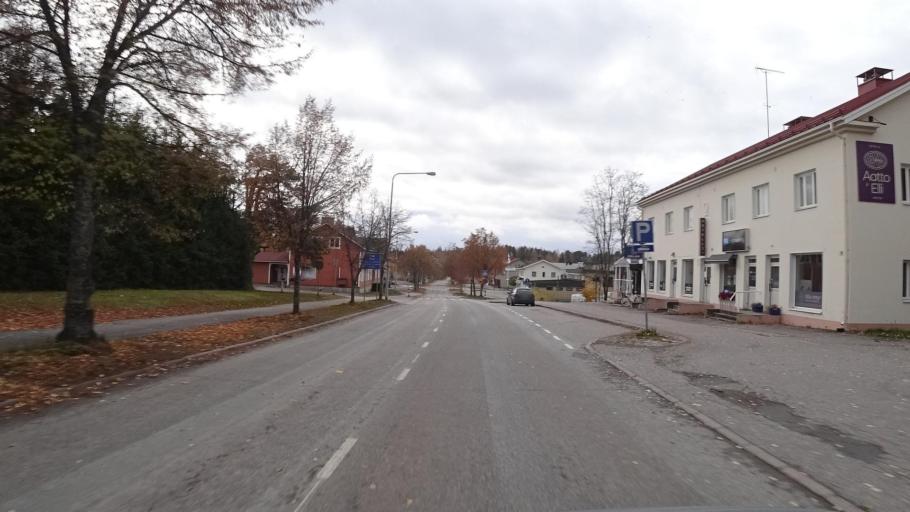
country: FI
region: Central Finland
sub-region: Joutsa
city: Joutsa
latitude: 61.7416
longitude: 26.1143
